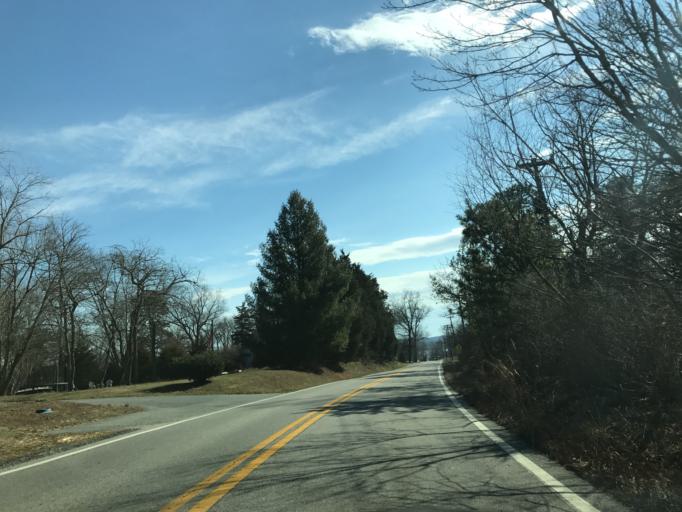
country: US
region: Maryland
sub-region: Cecil County
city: Charlestown
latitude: 39.5749
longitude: -75.9854
